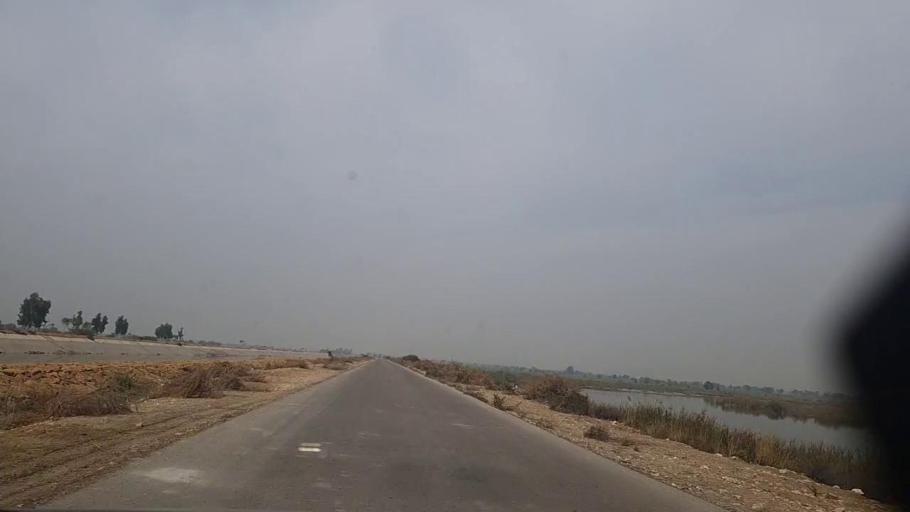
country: PK
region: Sindh
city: Sakrand
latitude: 26.2699
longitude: 68.2359
